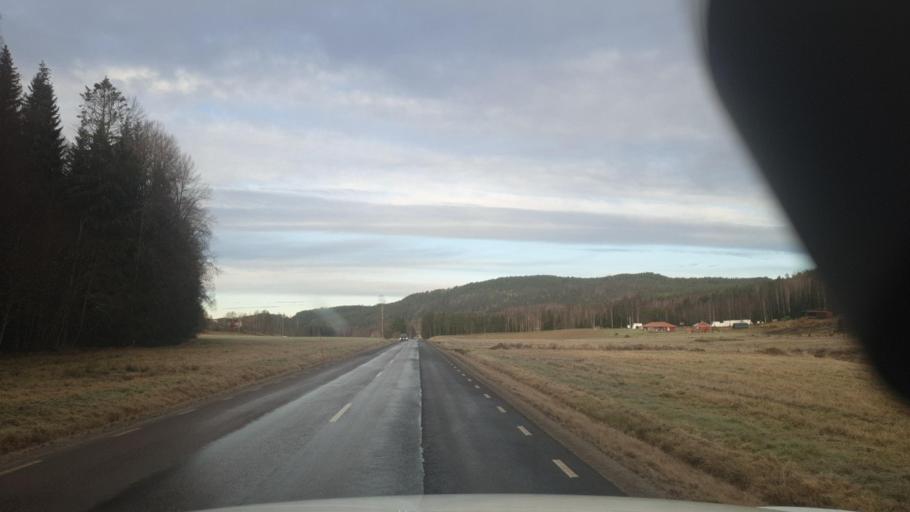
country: SE
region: Vaermland
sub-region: Arvika Kommun
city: Arvika
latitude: 59.7357
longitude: 12.6419
